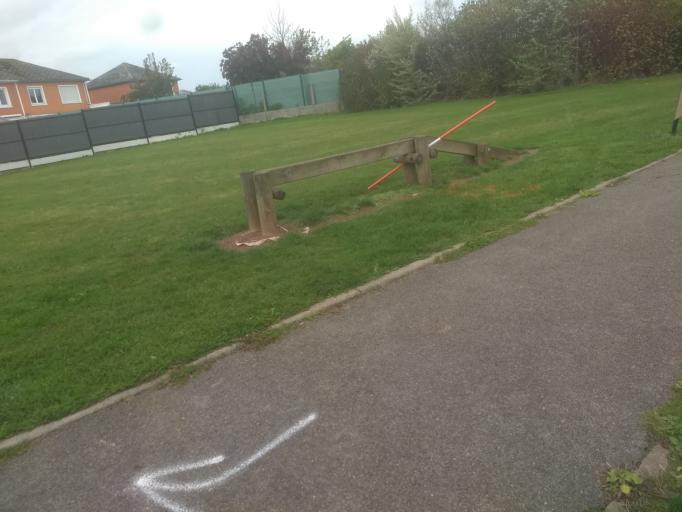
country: FR
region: Nord-Pas-de-Calais
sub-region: Departement du Pas-de-Calais
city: Beaurains
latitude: 50.2629
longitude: 2.7786
